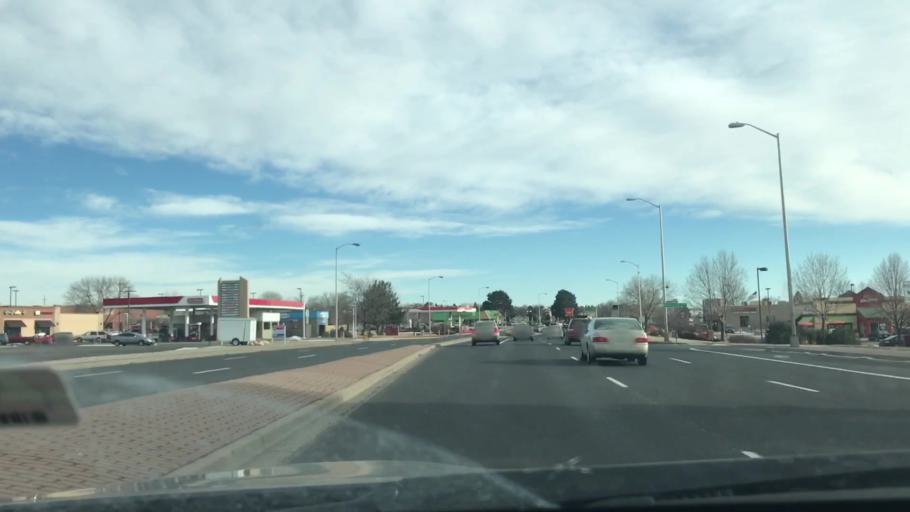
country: US
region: Colorado
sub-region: El Paso County
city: Cimarron Hills
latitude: 38.8953
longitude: -104.7593
